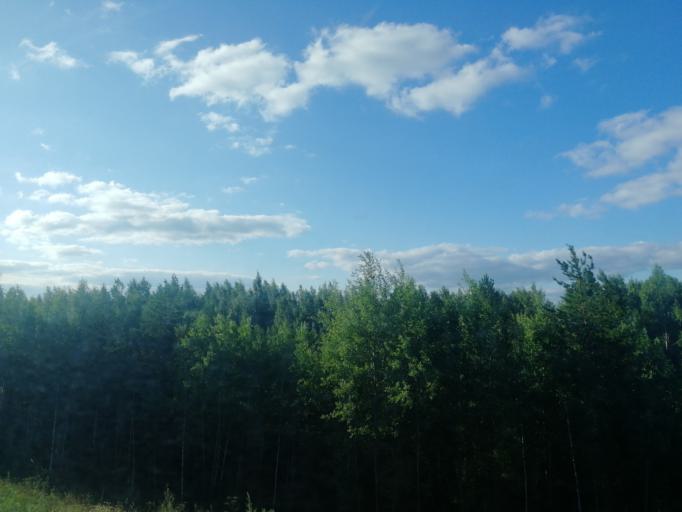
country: RU
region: Tula
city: Novogurovskiy
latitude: 54.2803
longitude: 37.2041
